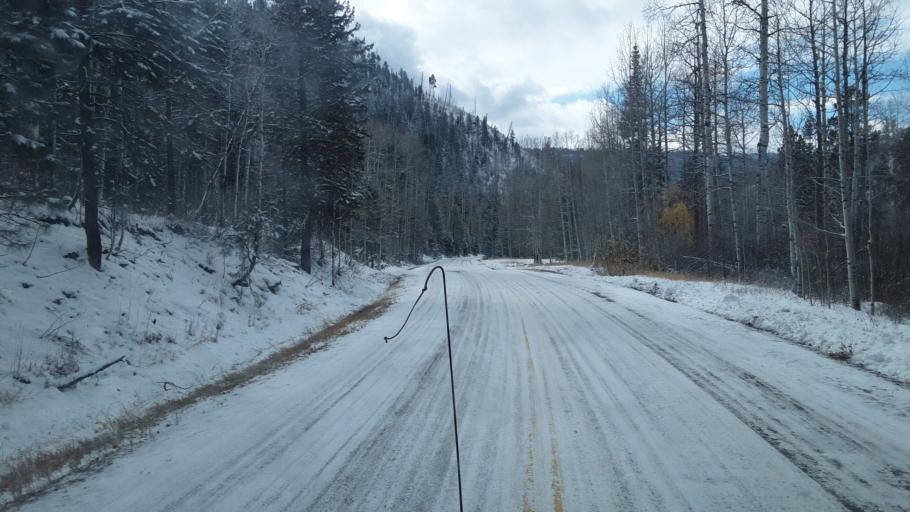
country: US
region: Colorado
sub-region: La Plata County
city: Bayfield
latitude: 37.3780
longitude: -107.6589
